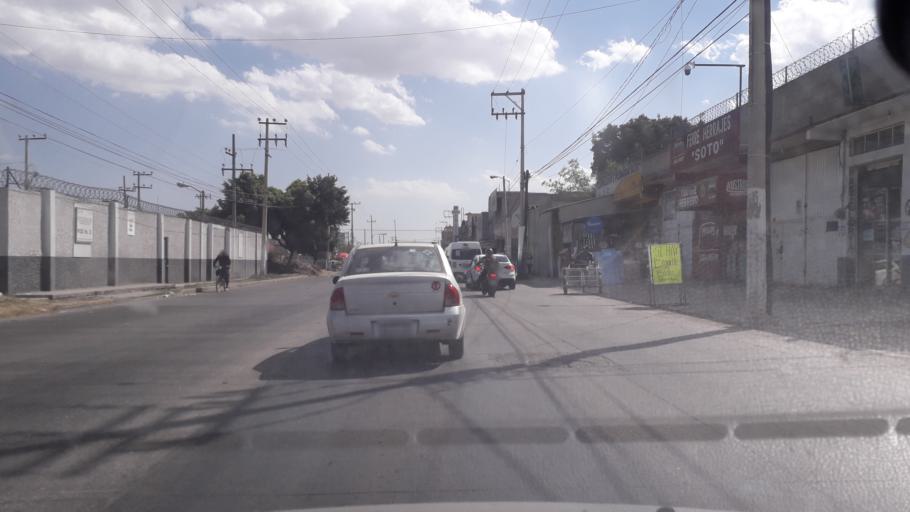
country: MX
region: Mexico
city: Ecatepec
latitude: 19.6308
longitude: -99.0523
